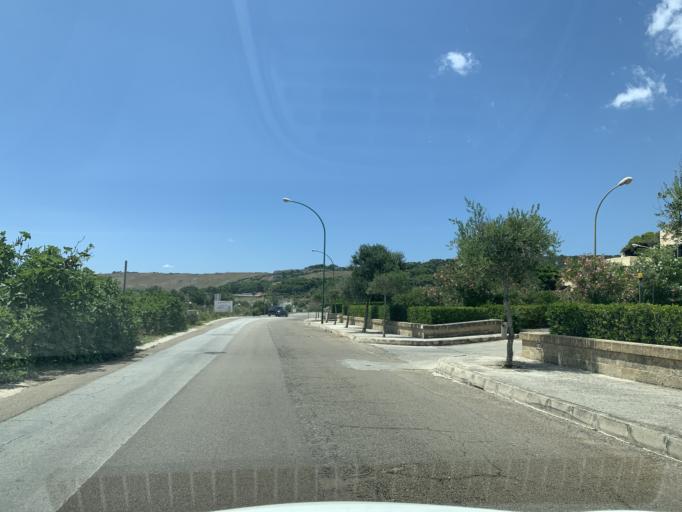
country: IT
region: Apulia
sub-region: Provincia di Lecce
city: Santa Cesarea Terme
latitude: 40.0327
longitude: 18.4503
